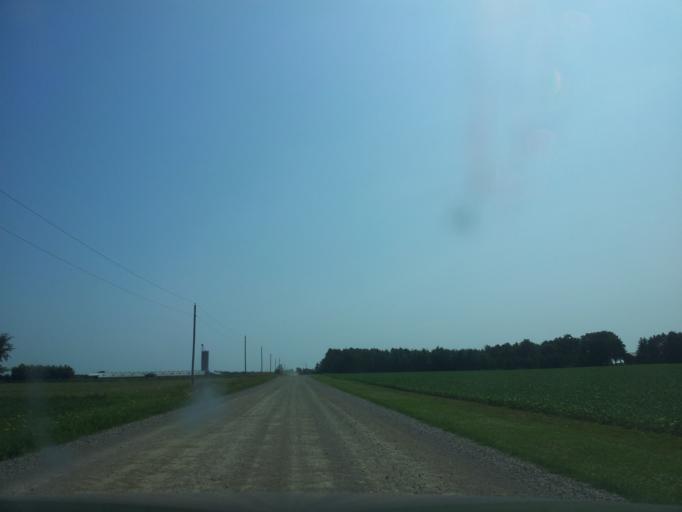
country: CA
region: Ontario
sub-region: Oxford County
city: Woodstock
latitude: 42.9488
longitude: -80.6547
